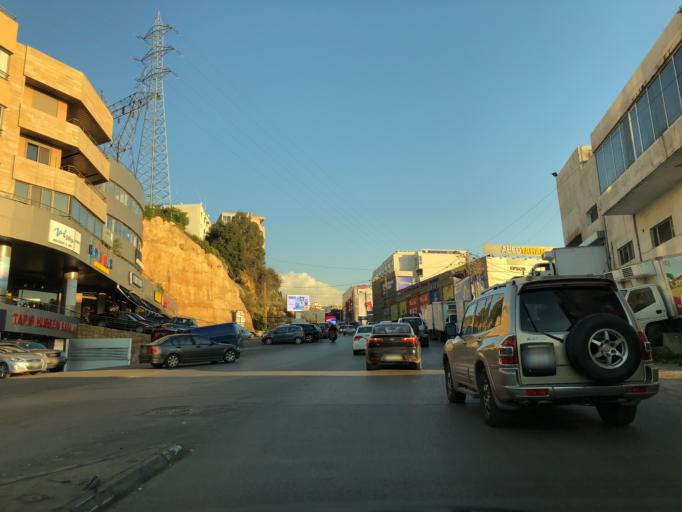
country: LB
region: Mont-Liban
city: Baabda
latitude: 33.8596
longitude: 35.5581
